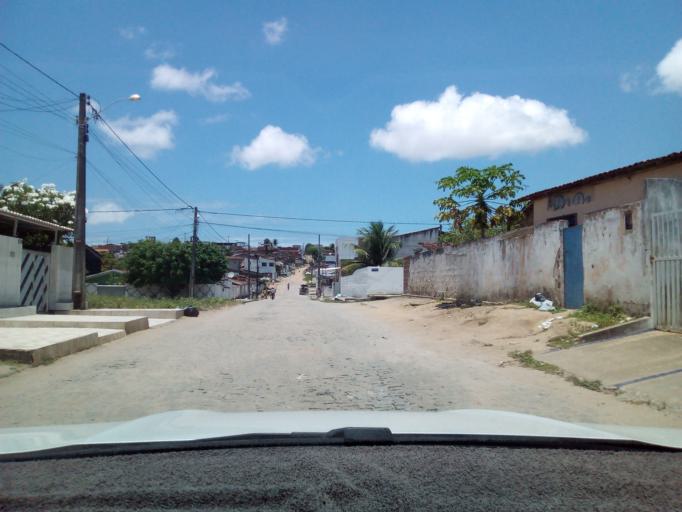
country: BR
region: Paraiba
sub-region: Joao Pessoa
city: Joao Pessoa
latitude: -7.1859
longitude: -34.8880
